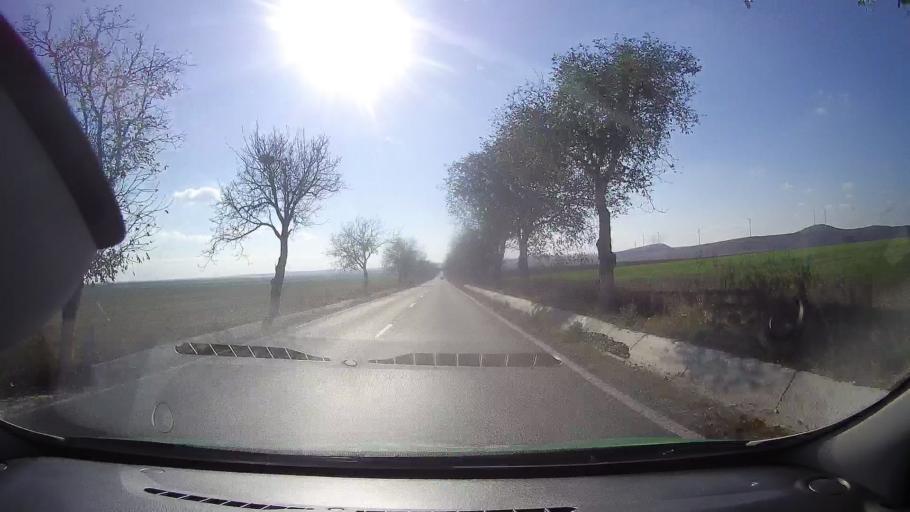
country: RO
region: Tulcea
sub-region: Comuna Ceamurlia de Jos
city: Ceamurlia de Jos
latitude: 44.8021
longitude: 28.6906
